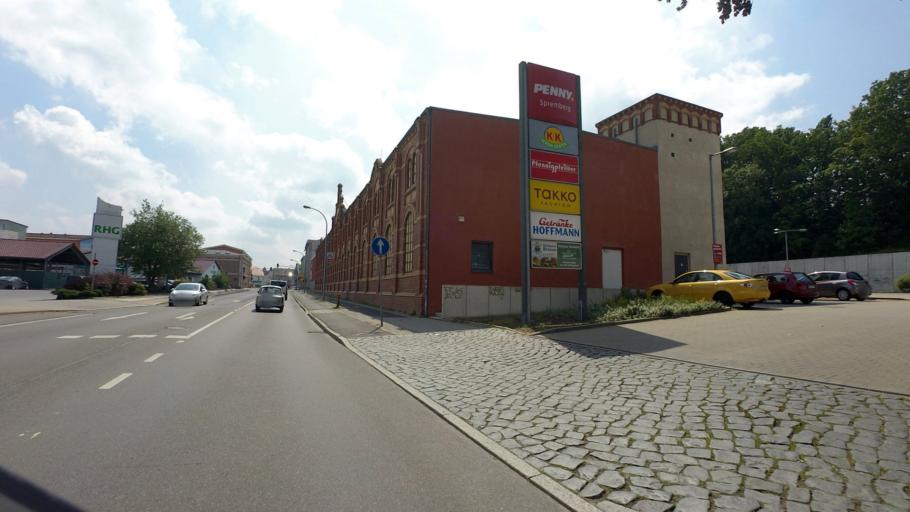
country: DE
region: Brandenburg
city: Spremberg
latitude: 51.5706
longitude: 14.3679
